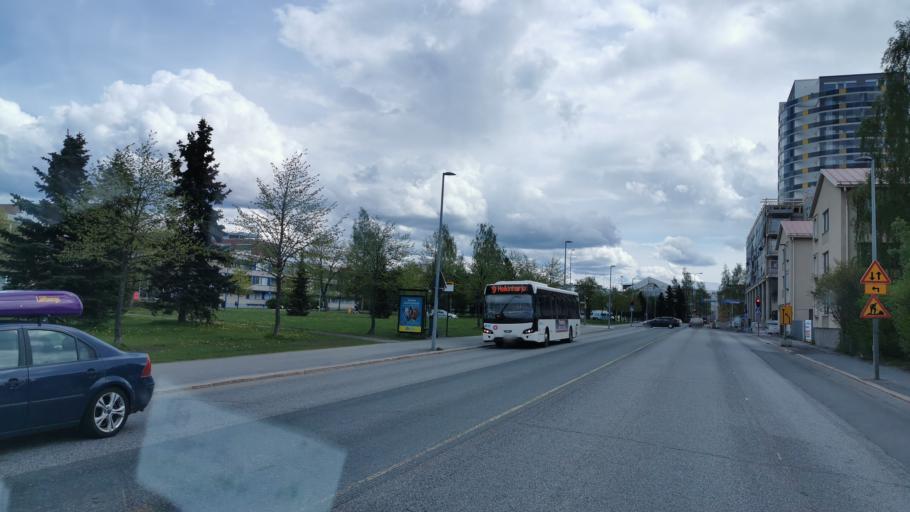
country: FI
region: Northern Ostrobothnia
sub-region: Oulu
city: Oulu
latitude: 65.0048
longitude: 25.4601
